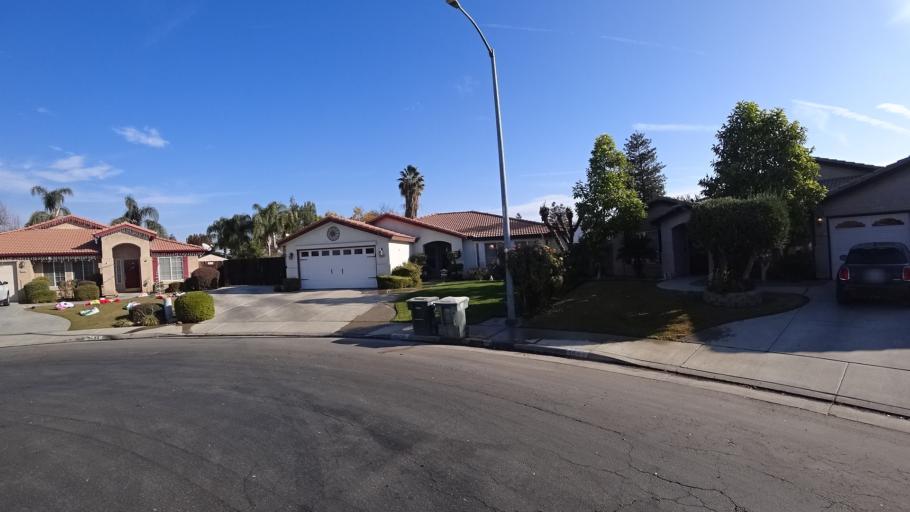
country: US
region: California
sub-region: Kern County
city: Oildale
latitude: 35.4042
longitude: -119.0642
